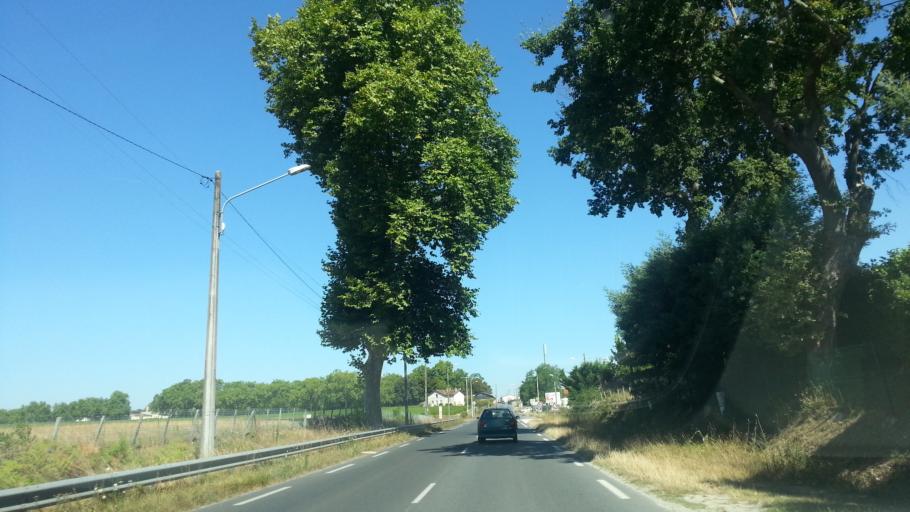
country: FR
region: Aquitaine
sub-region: Departement de la Gironde
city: Cadaujac
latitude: 44.7436
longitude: -0.5421
